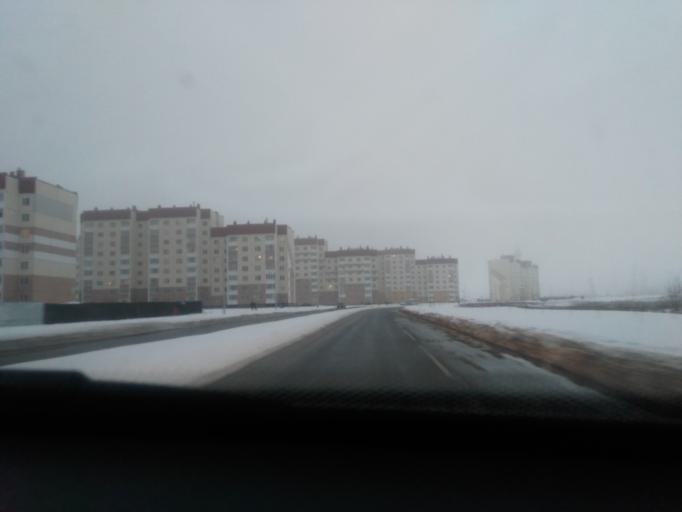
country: BY
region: Mogilev
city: Babruysk
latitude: 53.1997
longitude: 29.2246
